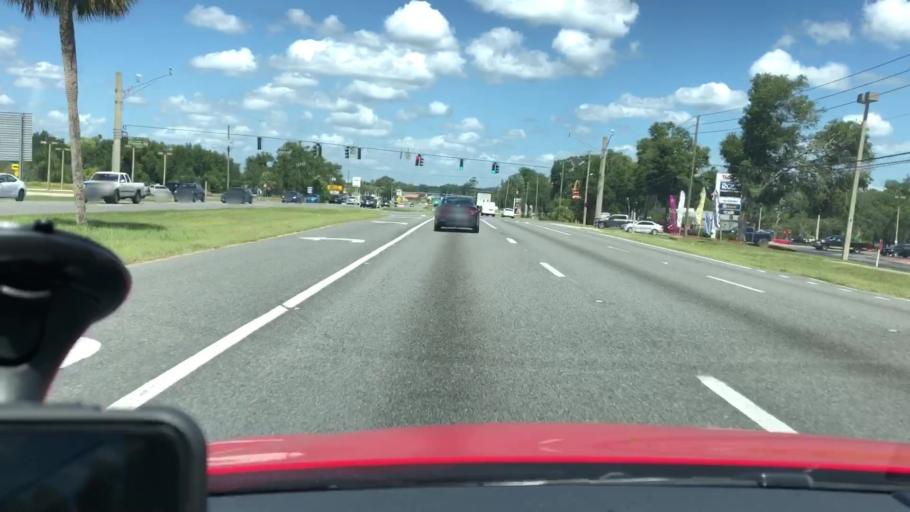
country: US
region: Florida
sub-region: Volusia County
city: De Land Southwest
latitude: 28.9799
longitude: -81.2994
